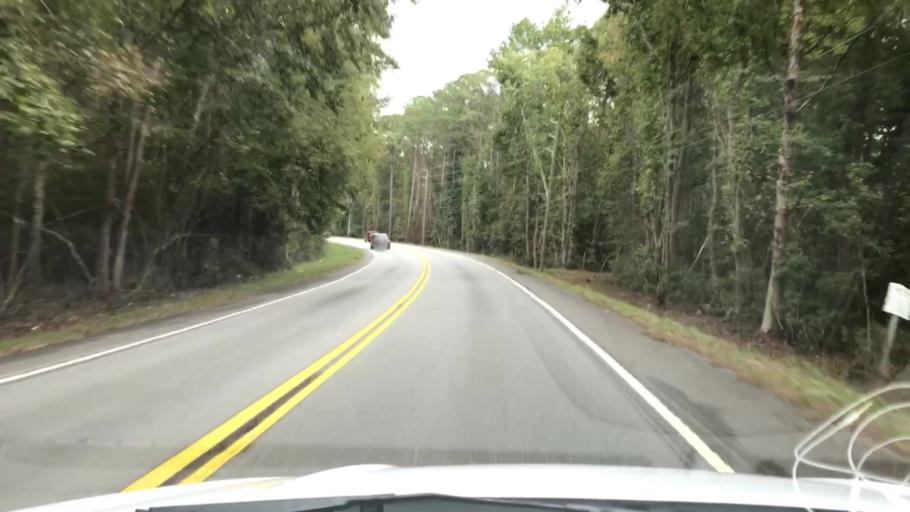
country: US
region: South Carolina
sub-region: Beaufort County
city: Bluffton
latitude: 32.2301
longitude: -80.9110
